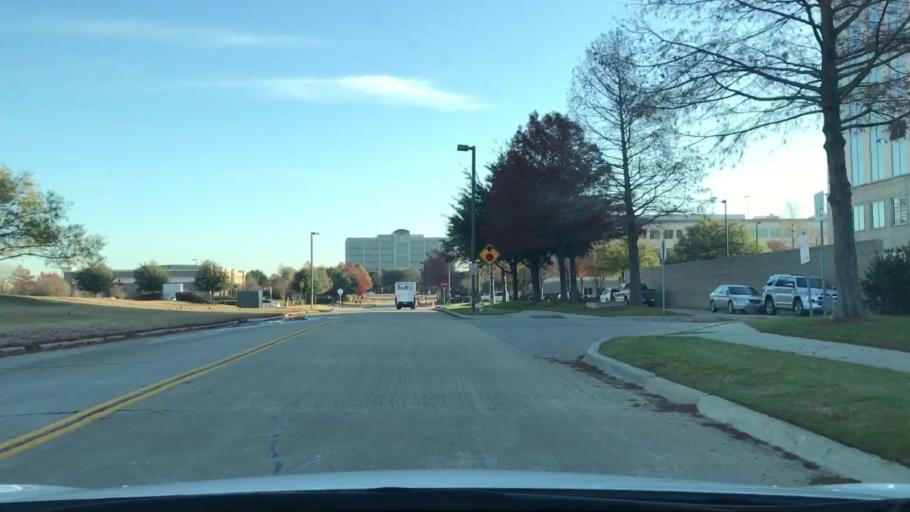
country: US
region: Texas
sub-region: Dallas County
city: Coppell
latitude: 32.8932
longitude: -96.9805
